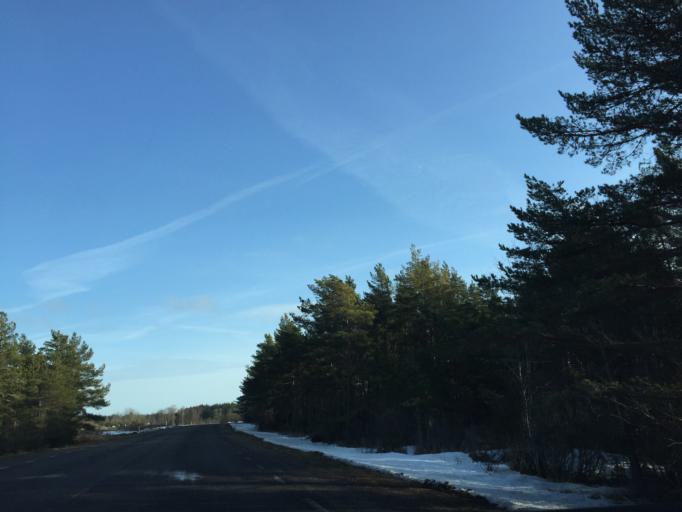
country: EE
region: Saare
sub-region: Kuressaare linn
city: Kuressaare
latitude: 58.4638
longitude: 21.9987
